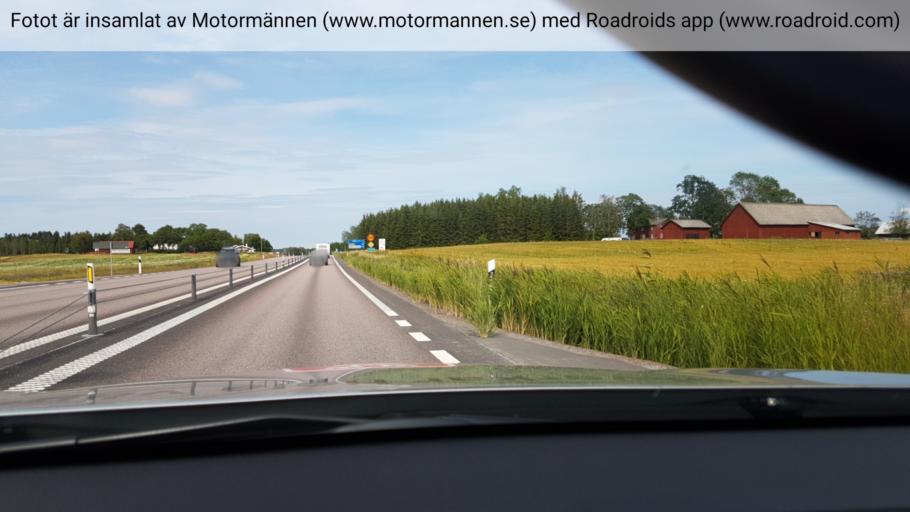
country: SE
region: Vaestra Goetaland
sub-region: Amals Kommun
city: Amal
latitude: 58.9622
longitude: 12.6104
